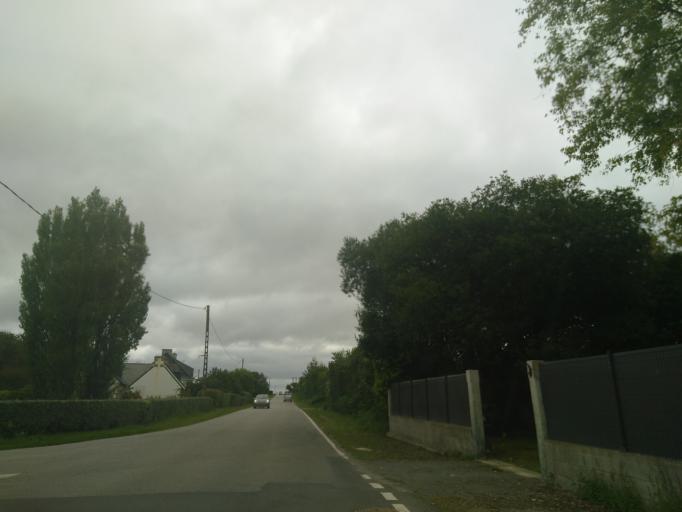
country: FR
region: Brittany
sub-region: Departement du Finistere
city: Plomodiern
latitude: 48.1683
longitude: -4.2737
